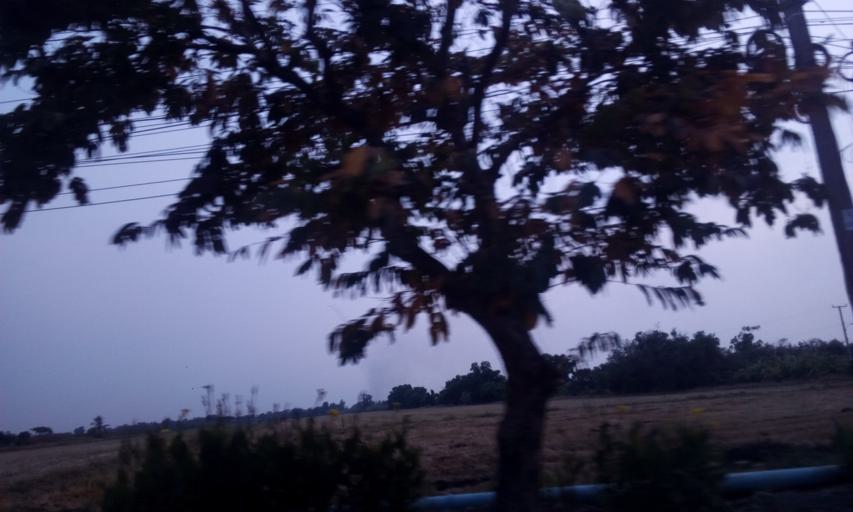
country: TH
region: Bangkok
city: Nong Chok
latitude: 13.8438
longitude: 100.8984
